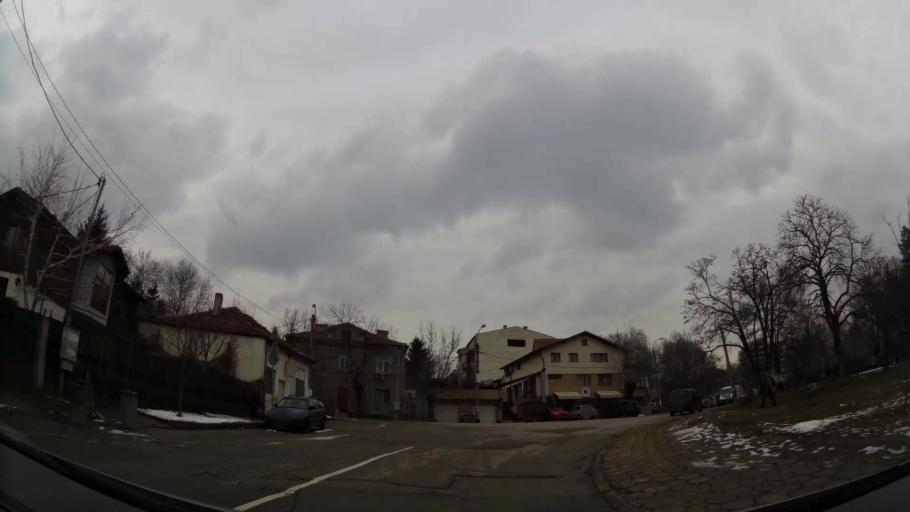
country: BG
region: Sofiya
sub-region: Obshtina Bozhurishte
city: Bozhurishte
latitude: 42.6757
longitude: 23.2367
